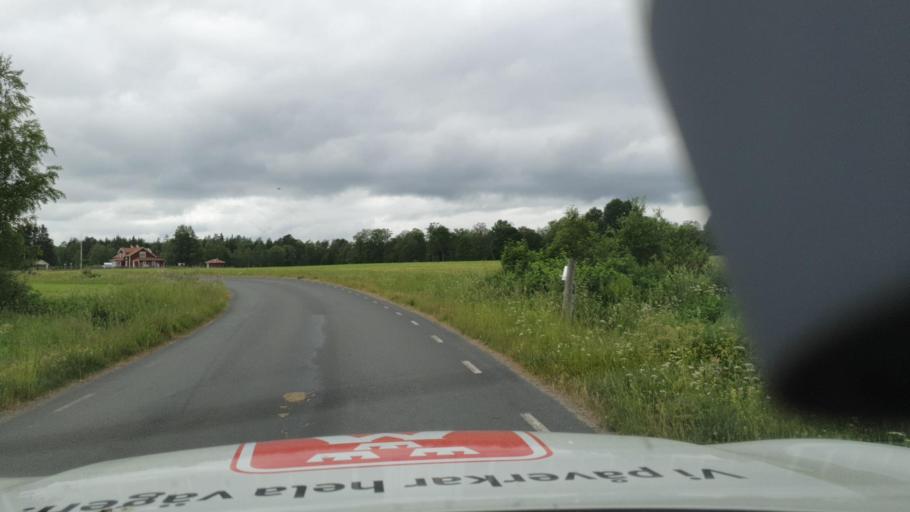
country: SE
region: Joenkoeping
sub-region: Mullsjo Kommun
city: Mullsjoe
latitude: 57.8852
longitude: 13.8123
